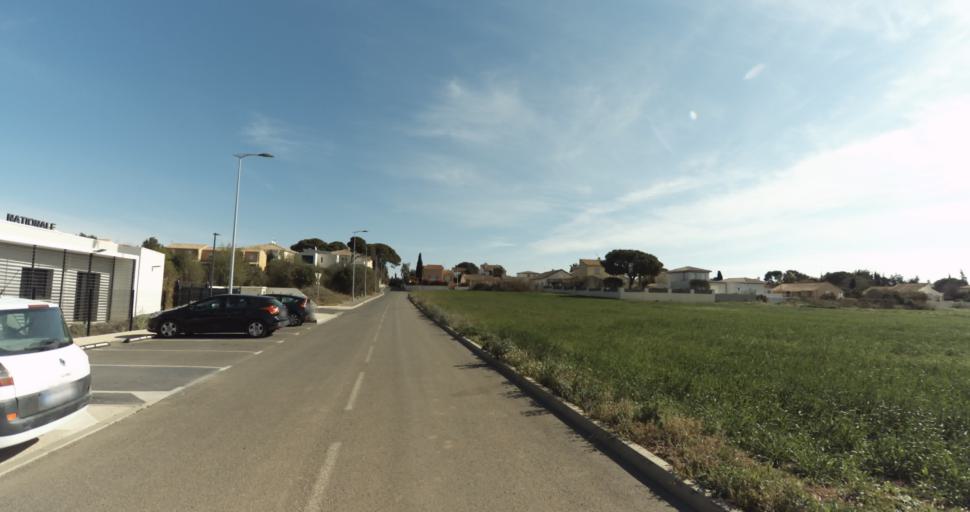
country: FR
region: Languedoc-Roussillon
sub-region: Departement de l'Herault
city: Marseillan
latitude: 43.3517
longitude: 3.5213
